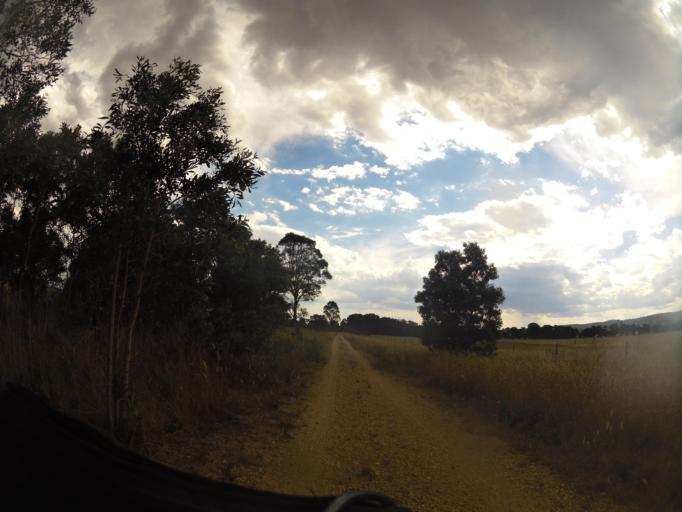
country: AU
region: Victoria
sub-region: Wellington
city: Heyfield
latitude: -38.0319
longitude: 146.6604
